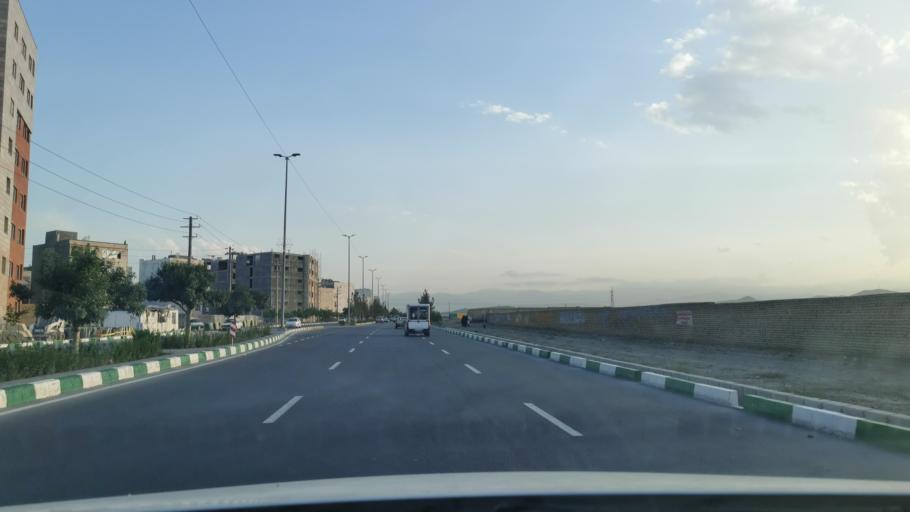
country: IR
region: Razavi Khorasan
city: Mashhad
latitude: 36.3940
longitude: 59.4729
